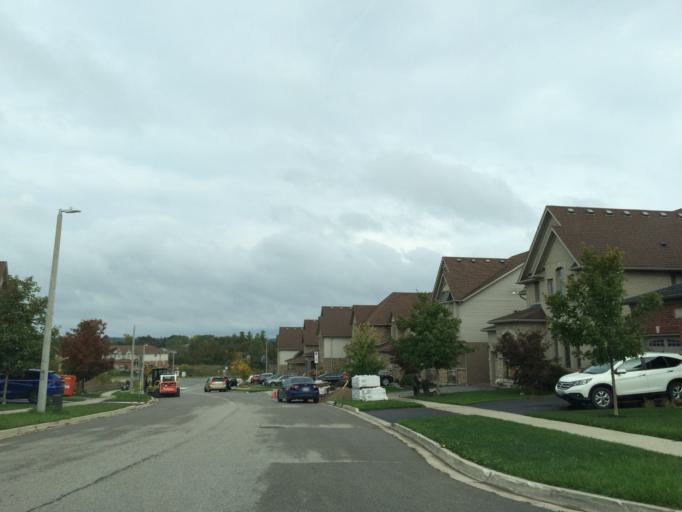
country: CA
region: Ontario
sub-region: Wellington County
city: Guelph
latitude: 43.5312
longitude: -80.2026
